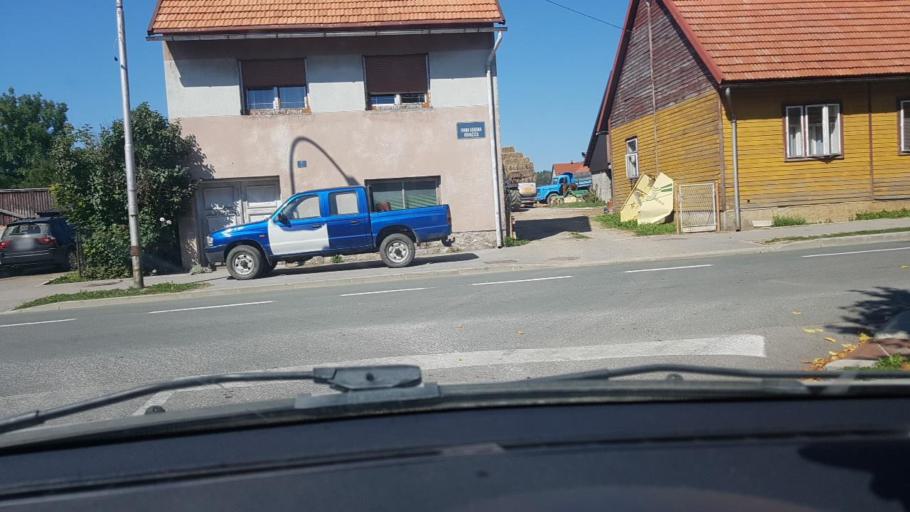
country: SI
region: Kostel
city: Kostel
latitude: 45.3736
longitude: 14.9386
